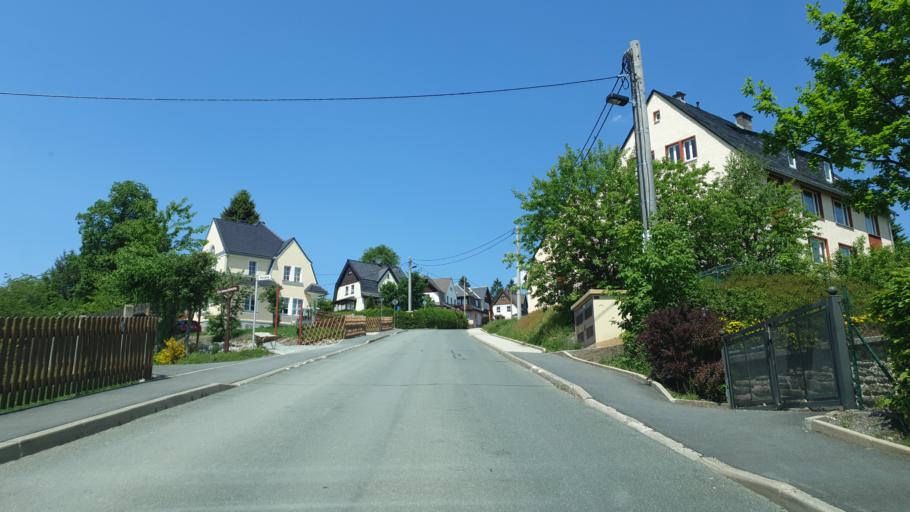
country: DE
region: Saxony
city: Klingenthal
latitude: 50.3583
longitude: 12.4654
